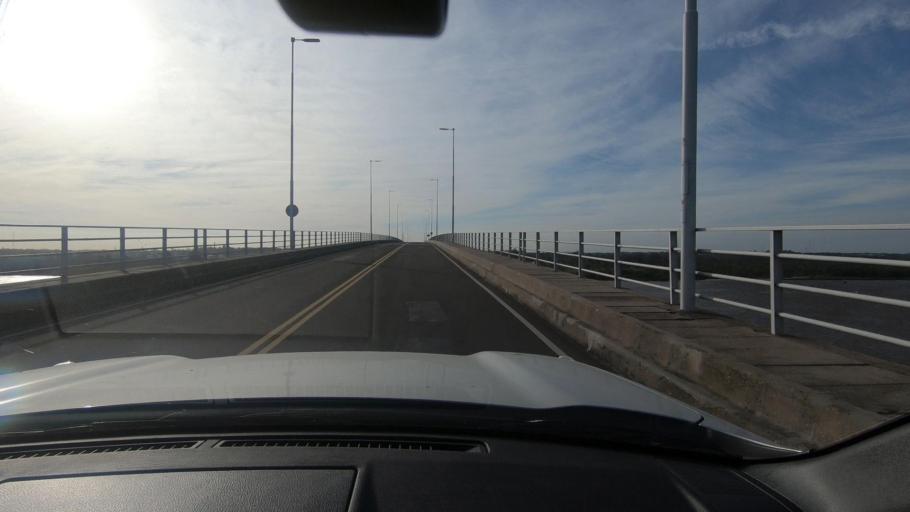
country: AR
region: Entre Rios
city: Colon
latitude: -32.2398
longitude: -58.1549
